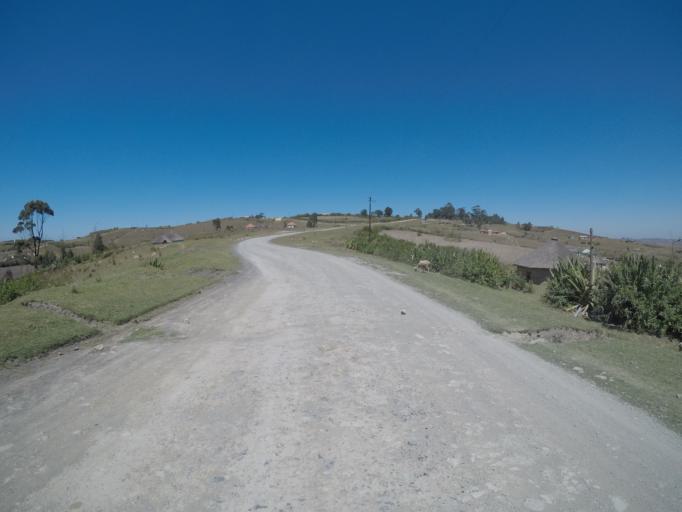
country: ZA
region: Eastern Cape
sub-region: OR Tambo District Municipality
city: Libode
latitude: -31.9788
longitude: 29.0350
